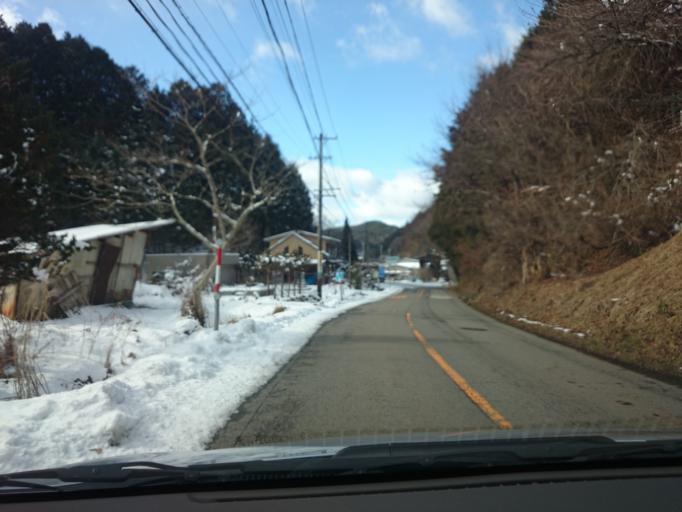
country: JP
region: Gifu
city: Gujo
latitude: 35.7383
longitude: 137.0116
